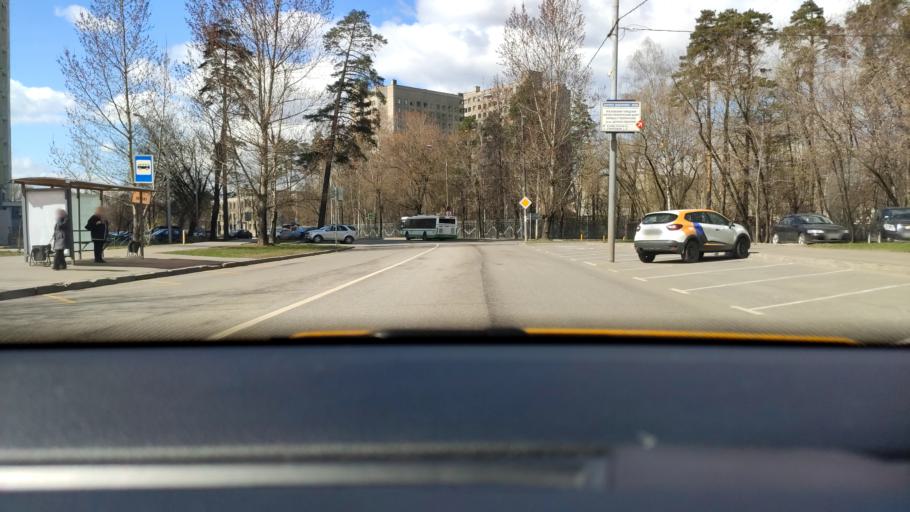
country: RU
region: Moscow
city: Yaroslavskiy
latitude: 55.8865
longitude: 37.7072
